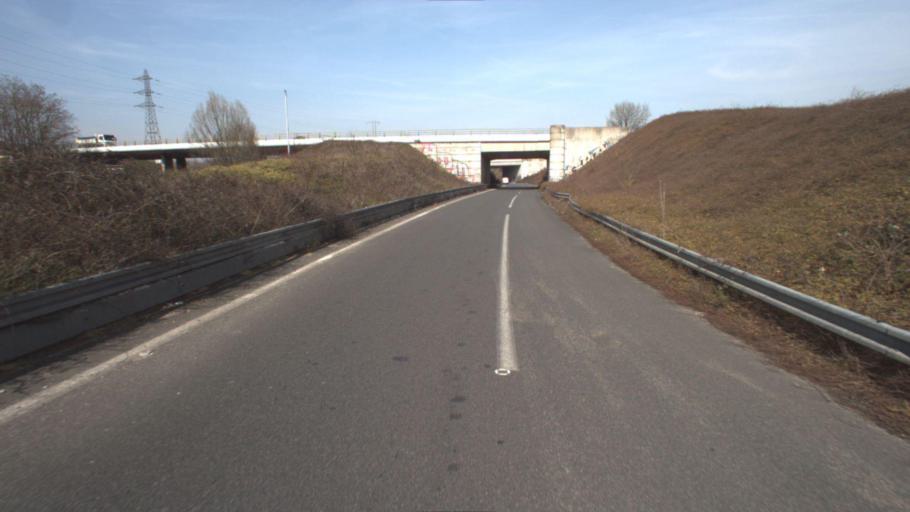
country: FR
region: Ile-de-France
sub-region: Departement de l'Essonne
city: Lisses
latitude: 48.6074
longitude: 2.4352
